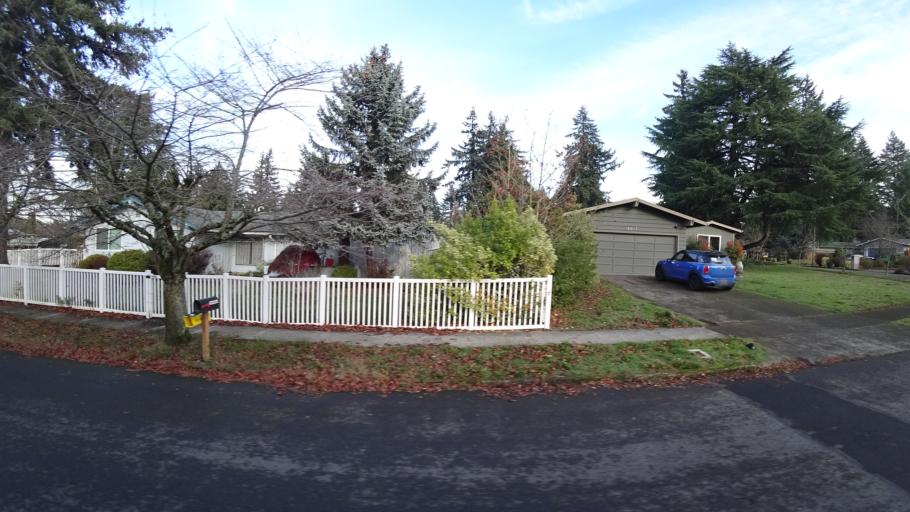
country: US
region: Oregon
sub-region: Multnomah County
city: Lents
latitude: 45.5288
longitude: -122.5294
